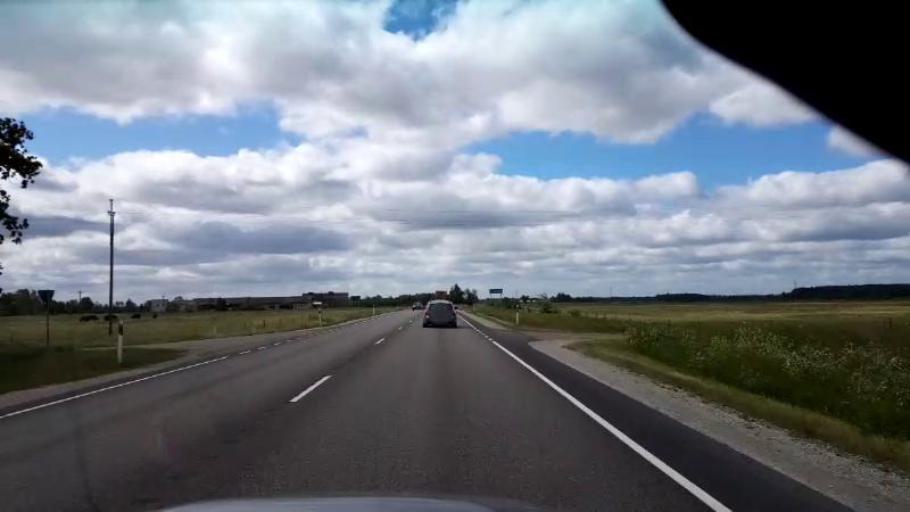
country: EE
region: Paernumaa
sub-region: Sauga vald
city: Sauga
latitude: 58.5147
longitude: 24.5546
